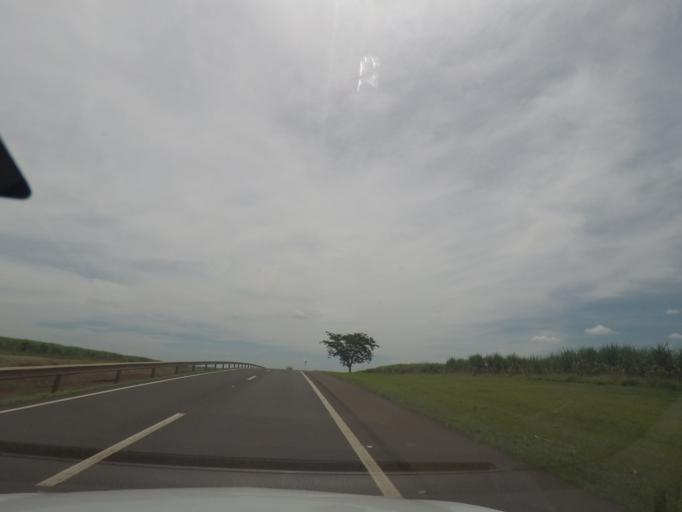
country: BR
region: Sao Paulo
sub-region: Bebedouro
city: Bebedouro
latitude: -21.0461
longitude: -48.4157
